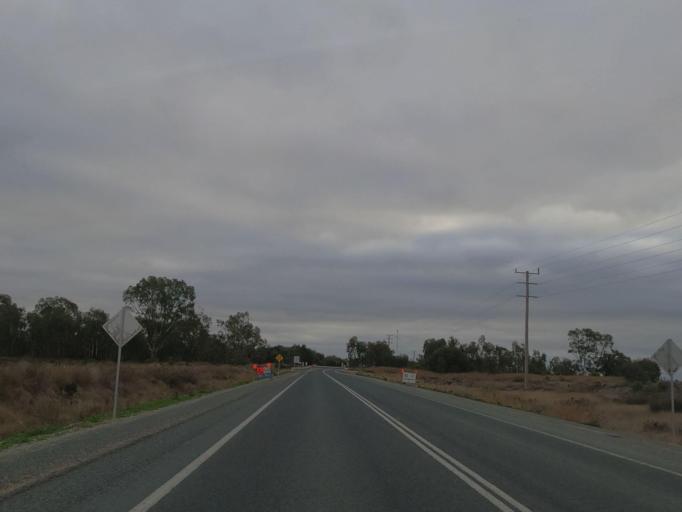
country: AU
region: Victoria
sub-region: Swan Hill
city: Swan Hill
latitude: -35.5372
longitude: 143.7474
